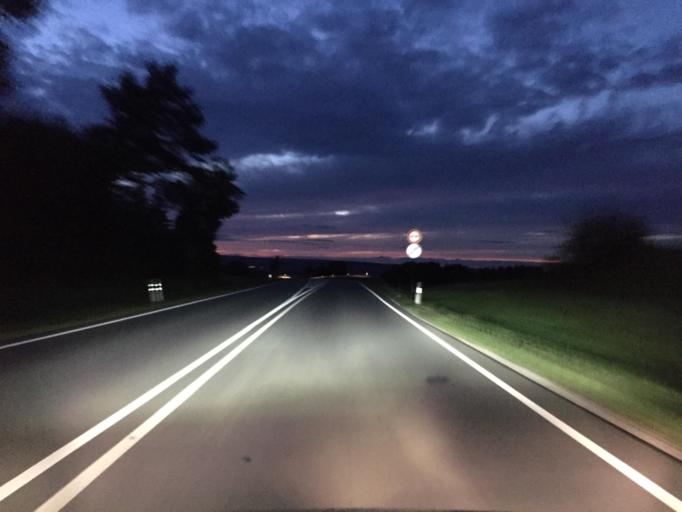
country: DE
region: Baden-Wuerttemberg
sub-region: Freiburg Region
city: Blumberg
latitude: 47.8847
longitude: 8.5296
